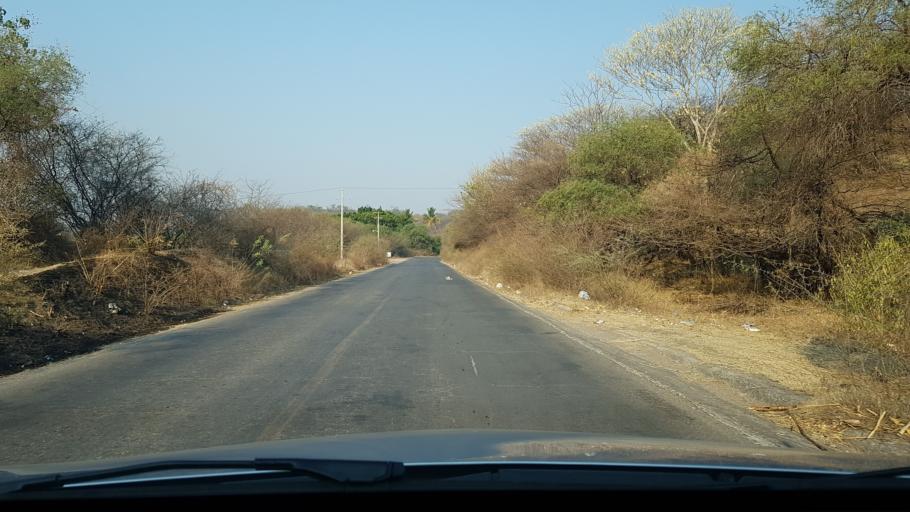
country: MX
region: Morelos
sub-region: Tepalcingo
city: Zacapalco
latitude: 18.6372
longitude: -99.0142
